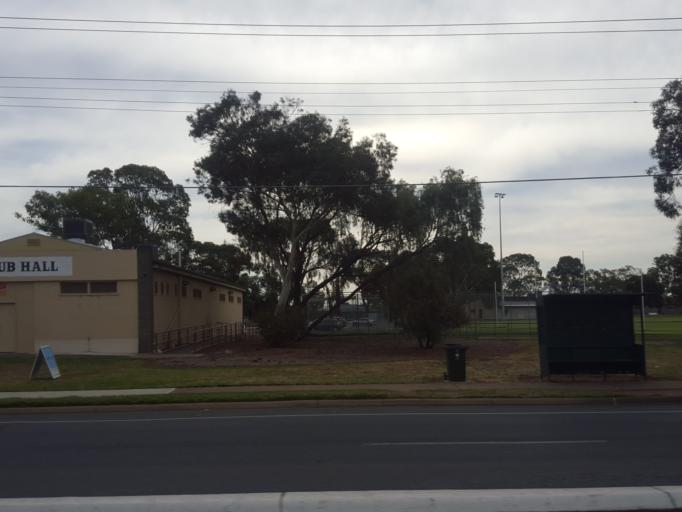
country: AU
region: South Australia
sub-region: Charles Sturt
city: Woodville North
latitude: -34.8612
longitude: 138.5475
